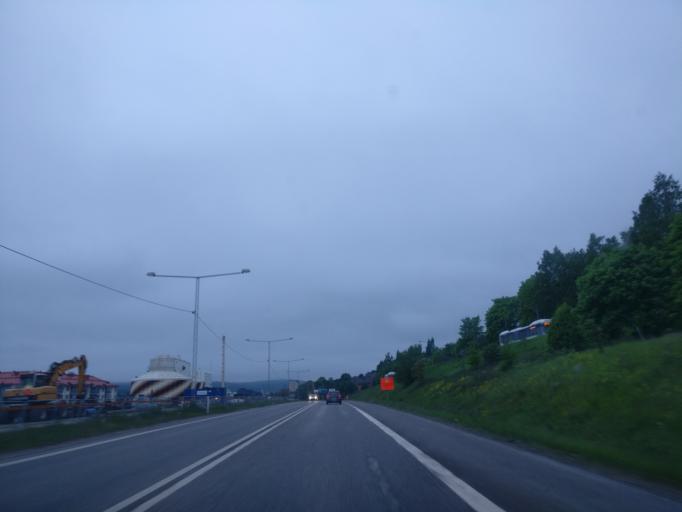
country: SE
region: Vaesternorrland
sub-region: Sundsvalls Kommun
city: Sundsvall
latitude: 62.3951
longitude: 17.3225
